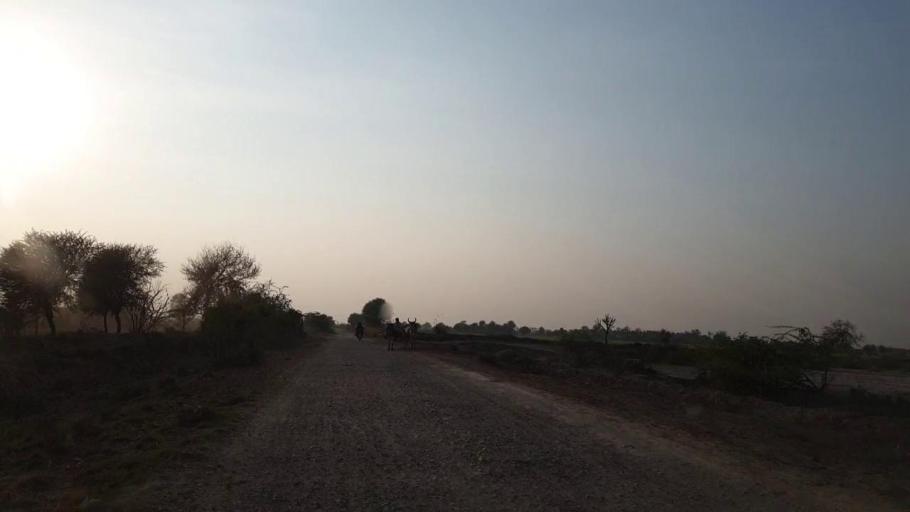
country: PK
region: Sindh
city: Pithoro
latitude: 25.6542
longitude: 69.2242
